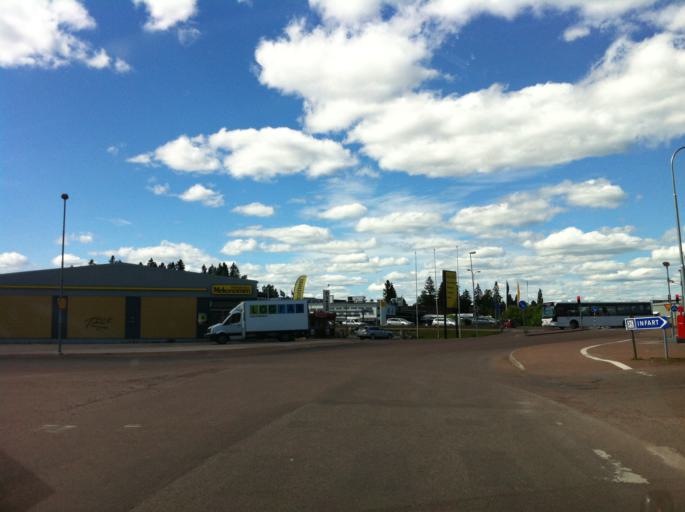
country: SE
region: Dalarna
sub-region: Mora Kommun
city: Mora
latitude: 61.0076
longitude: 14.5665
